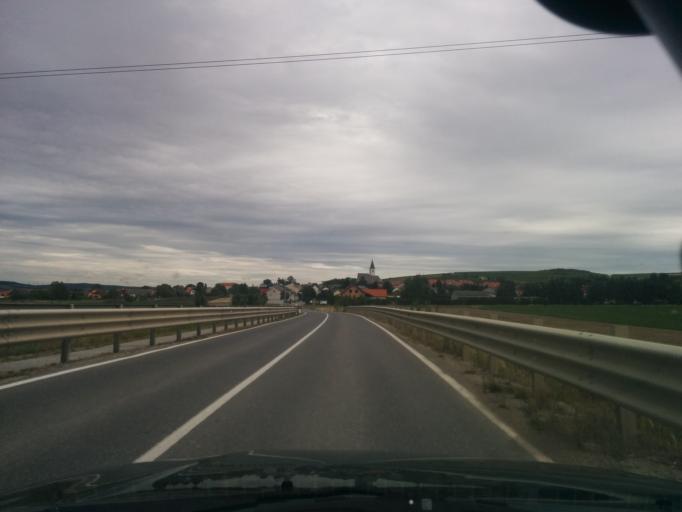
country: AT
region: Lower Austria
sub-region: Politischer Bezirk Korneuburg
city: Stetten
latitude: 48.3608
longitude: 16.3830
